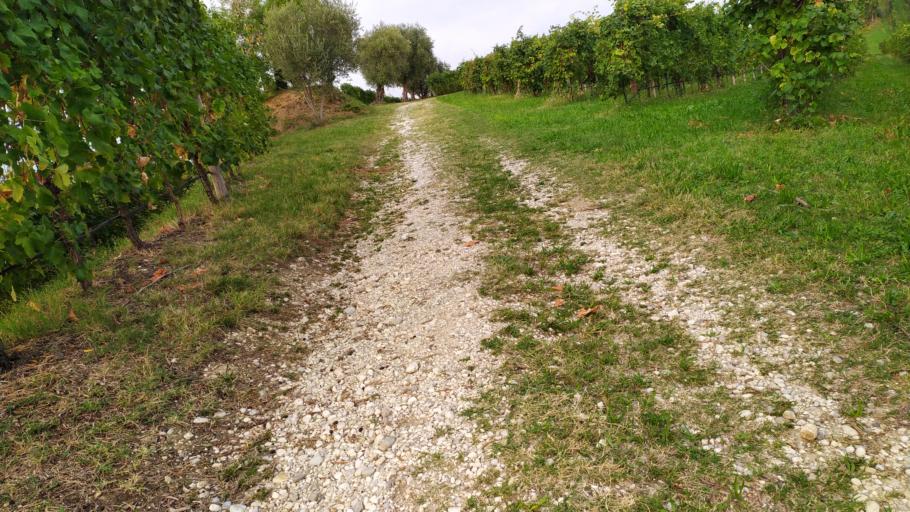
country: IT
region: Veneto
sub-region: Provincia di Treviso
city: Conegliano
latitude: 45.8869
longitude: 12.2781
